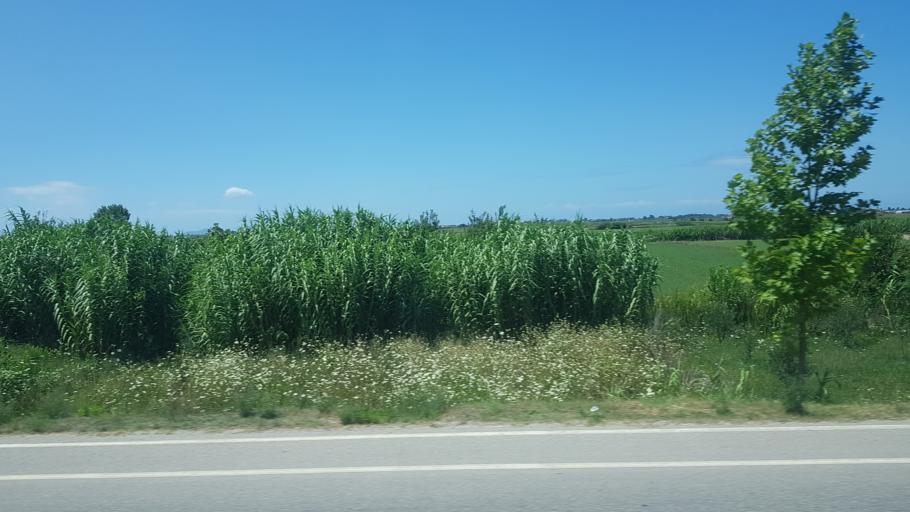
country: AL
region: Fier
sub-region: Rrethi i Fierit
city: Frakulla e Madhe
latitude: 40.6549
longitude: 19.4920
